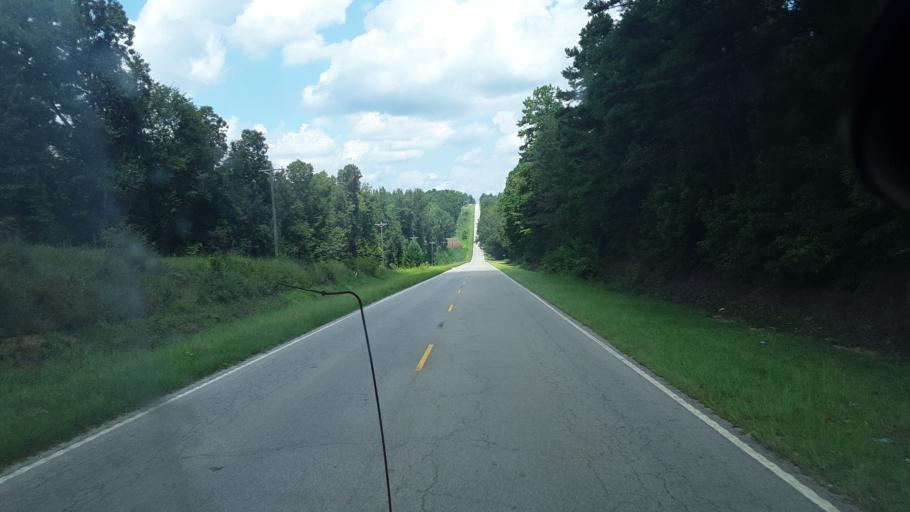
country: US
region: South Carolina
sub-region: Calhoun County
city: Oak Grove
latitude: 33.7335
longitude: -80.9577
